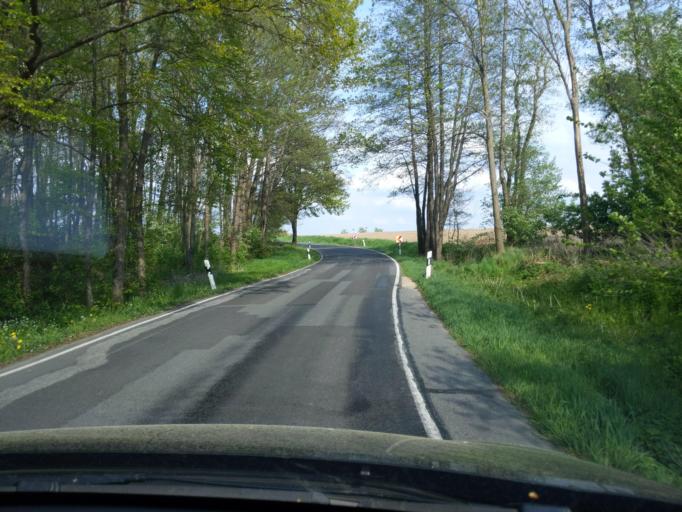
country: DE
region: Saxony
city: Kubschutz
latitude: 51.1954
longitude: 14.5015
